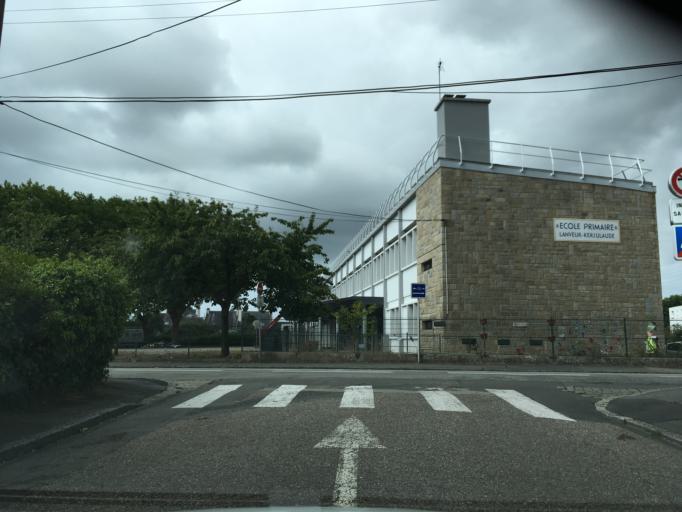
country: FR
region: Brittany
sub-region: Departement du Morbihan
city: Lorient
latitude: 47.7410
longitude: -3.3849
